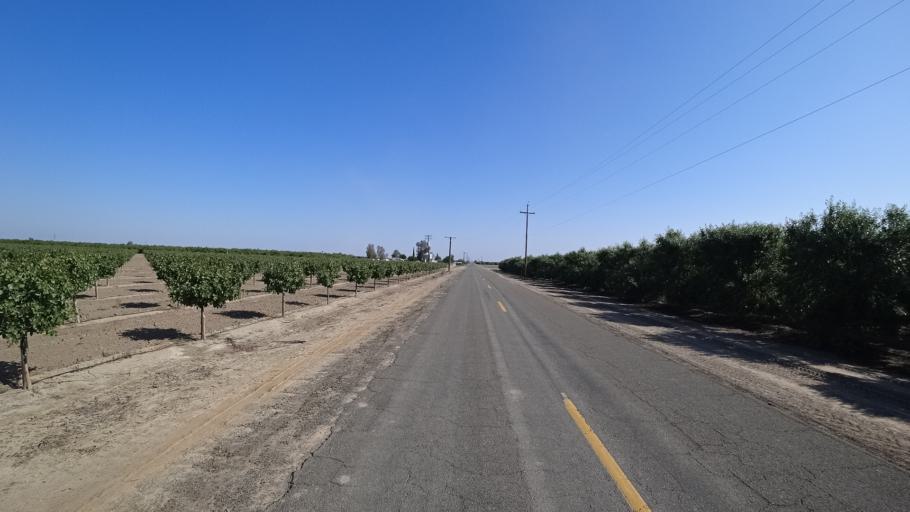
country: US
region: California
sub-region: Kings County
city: Home Garden
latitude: 36.2171
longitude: -119.5830
